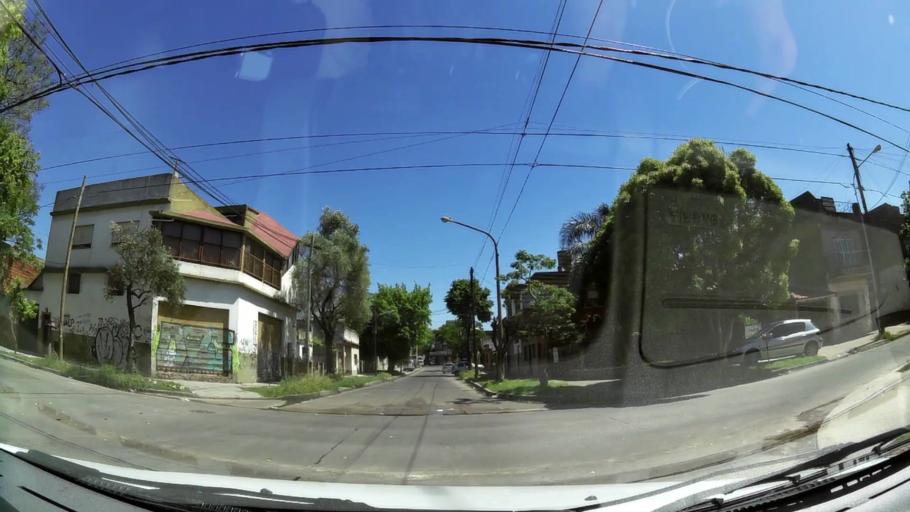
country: AR
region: Buenos Aires
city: Caseros
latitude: -34.5760
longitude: -58.5639
